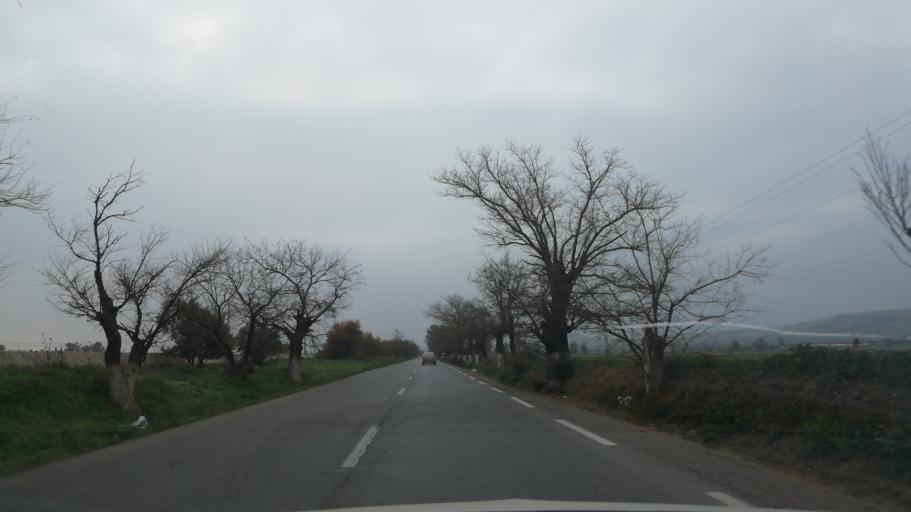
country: DZ
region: Sidi Bel Abbes
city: Sfizef
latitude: 35.2223
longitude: -0.2872
